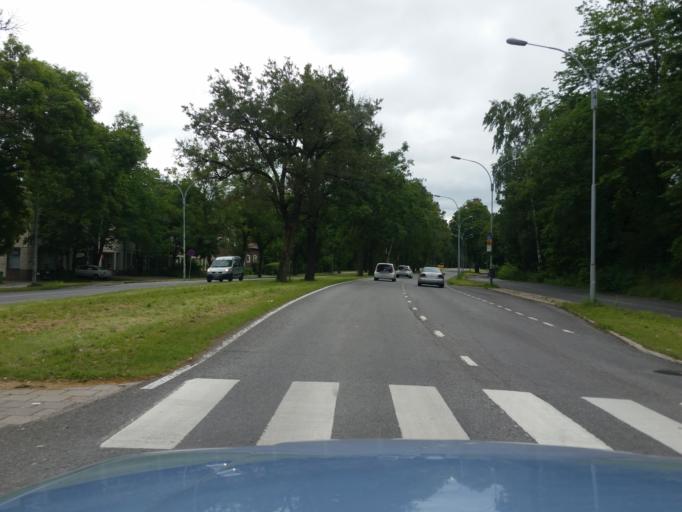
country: FI
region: Varsinais-Suomi
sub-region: Turku
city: Turku
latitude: 60.4413
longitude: 22.2893
